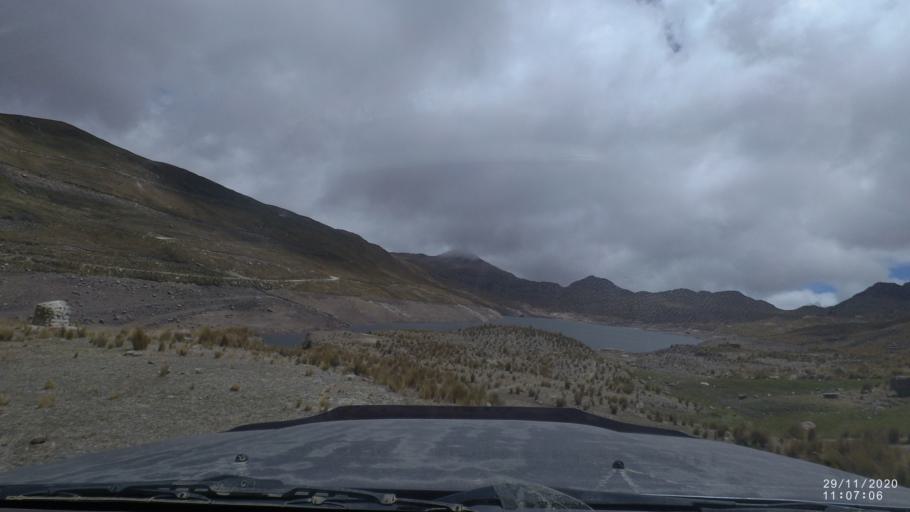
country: BO
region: Cochabamba
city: Cochabamba
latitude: -17.1864
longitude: -66.2078
